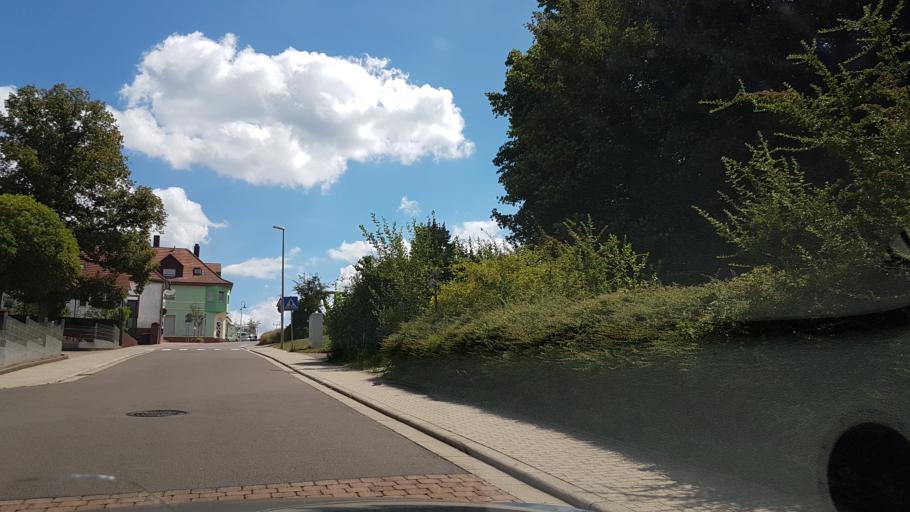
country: DE
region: Saarland
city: Illingen
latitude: 49.3701
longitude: 7.0847
